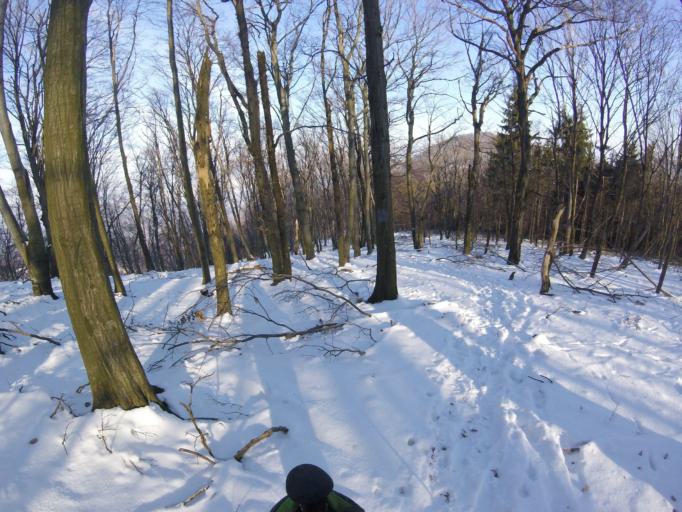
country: HU
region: Heves
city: Parad
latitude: 47.8727
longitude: 20.0662
